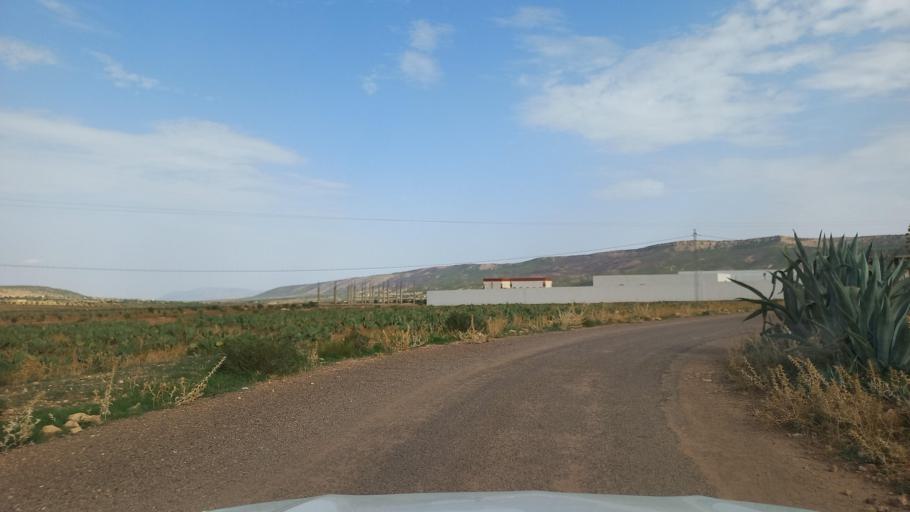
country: TN
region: Al Qasrayn
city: Kasserine
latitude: 35.3544
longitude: 8.8275
